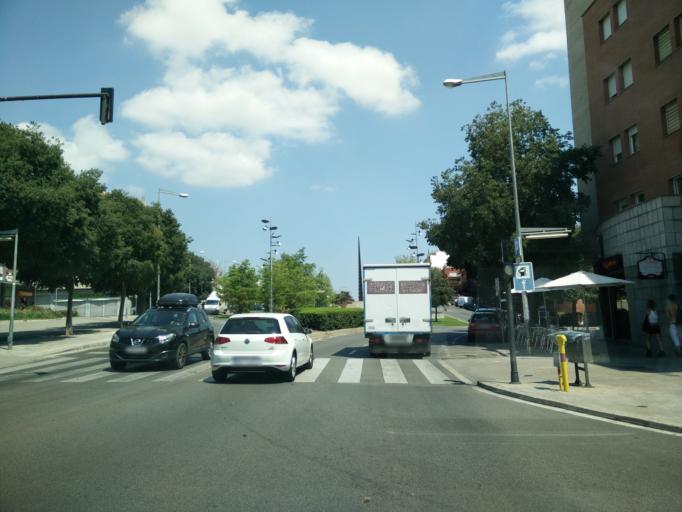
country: ES
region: Catalonia
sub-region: Provincia de Barcelona
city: Terrassa
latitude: 41.5692
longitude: 2.0220
